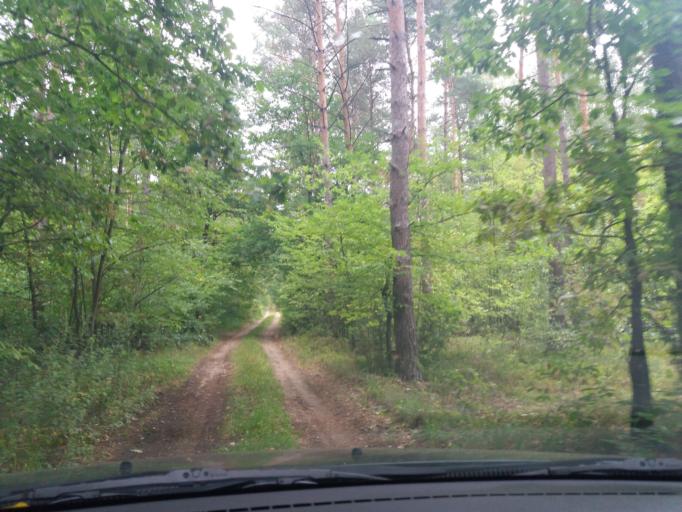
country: PL
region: Masovian Voivodeship
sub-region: Powiat mlawski
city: Wieczfnia Koscielna
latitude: 53.2303
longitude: 20.4768
